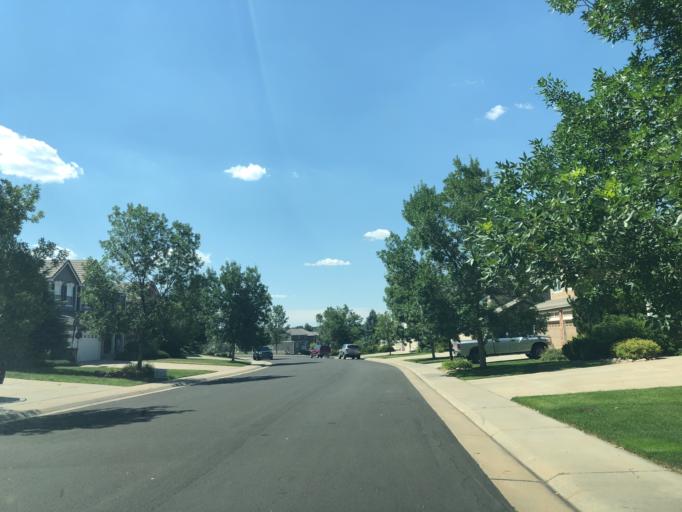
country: US
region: Colorado
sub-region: Arapahoe County
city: Dove Valley
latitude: 39.6066
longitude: -104.7835
